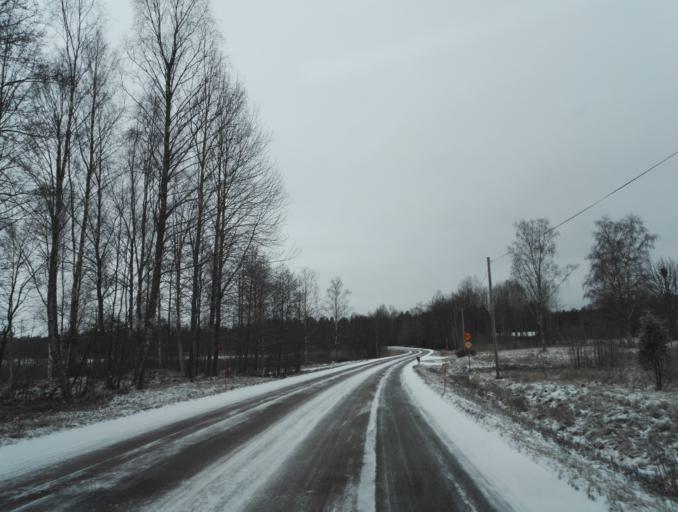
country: SE
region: Kronoberg
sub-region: Lessebo Kommun
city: Hovmantorp
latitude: 56.6678
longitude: 15.1579
